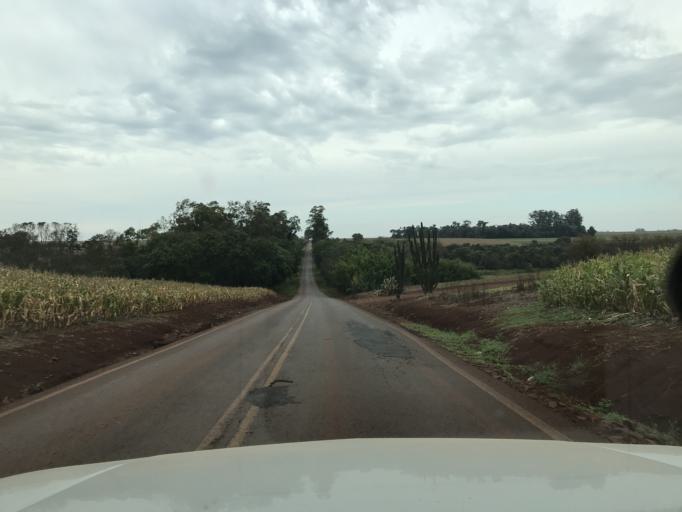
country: BR
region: Parana
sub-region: Palotina
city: Palotina
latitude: -24.4292
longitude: -53.9091
